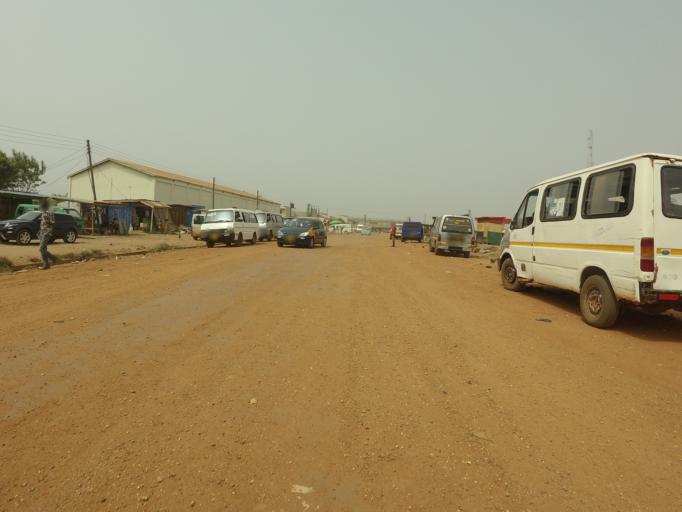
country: GH
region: Greater Accra
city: Medina Estates
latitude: 5.6363
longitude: -0.1262
